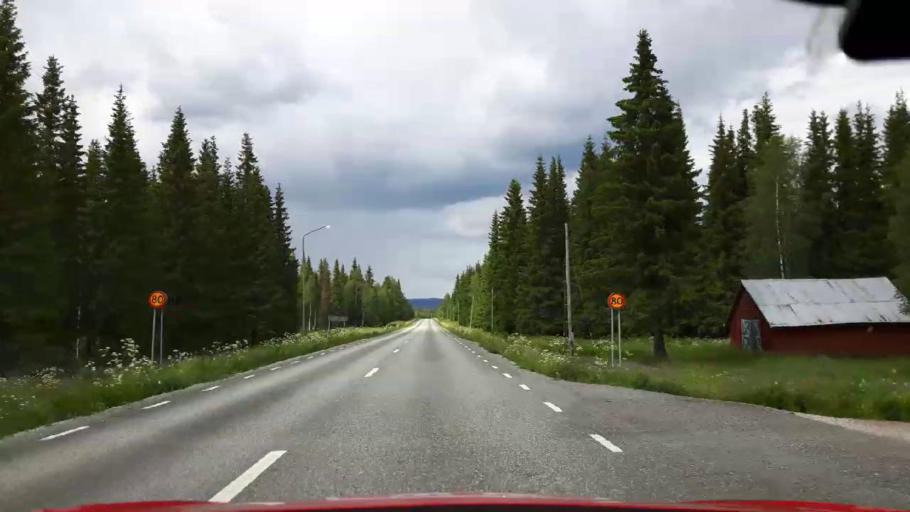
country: SE
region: Jaemtland
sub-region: Krokoms Kommun
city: Krokom
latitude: 63.6488
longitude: 14.3786
